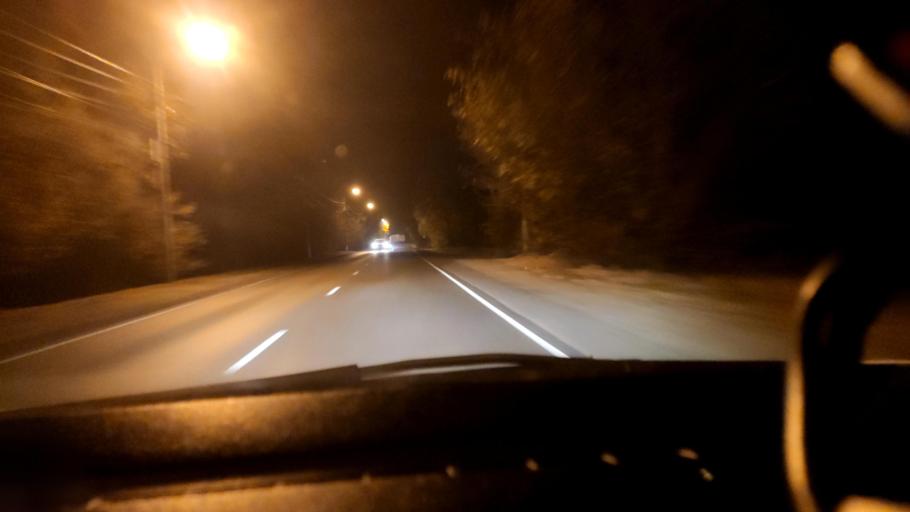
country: RU
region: Voronezj
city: Pridonskoy
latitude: 51.6356
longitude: 39.0851
